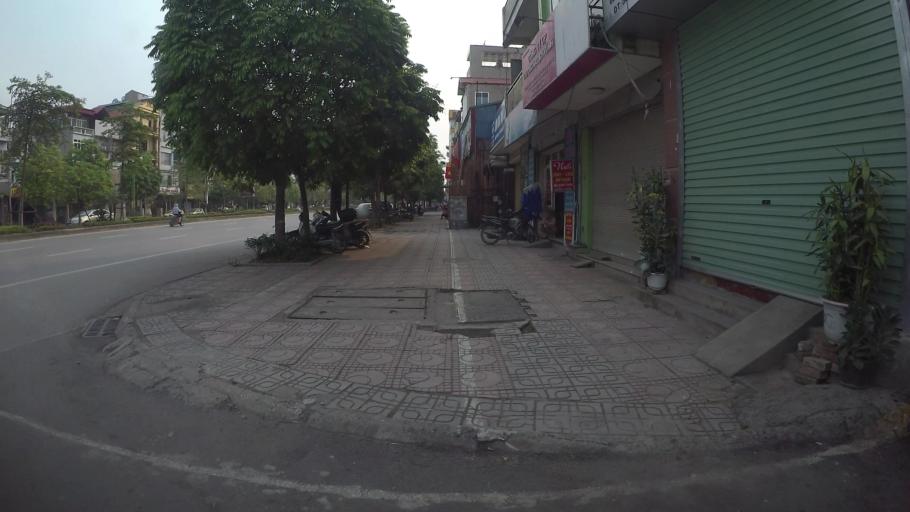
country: VN
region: Ha Noi
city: Trau Quy
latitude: 21.0729
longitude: 105.9049
